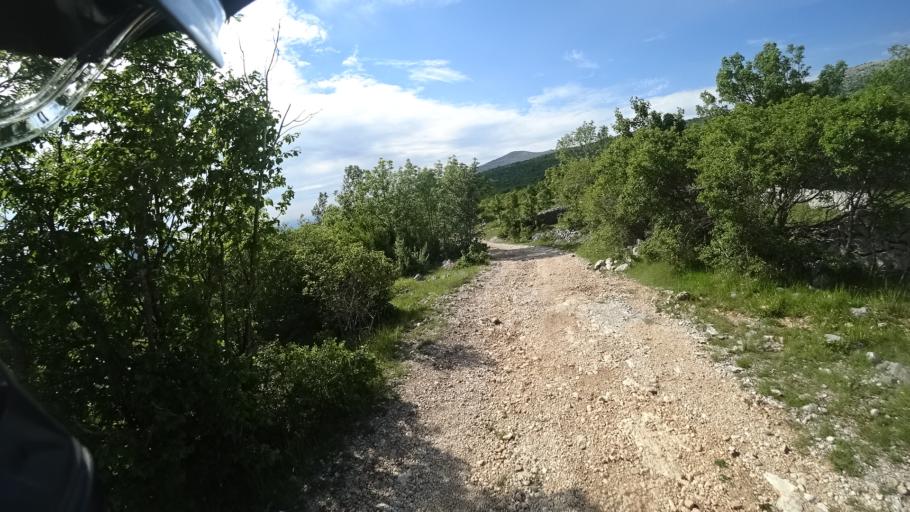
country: HR
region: Splitsko-Dalmatinska
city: Hrvace
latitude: 43.7799
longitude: 16.4481
